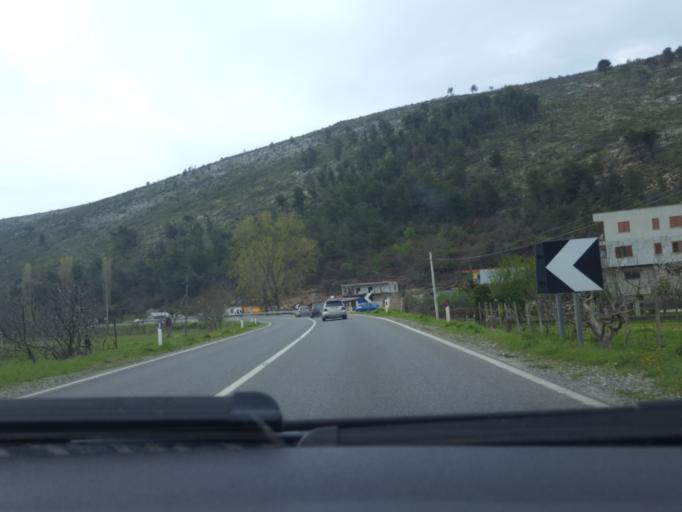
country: AL
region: Lezhe
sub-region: Rrethi i Lezhes
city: Balldreni i Ri
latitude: 41.8034
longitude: 19.6308
